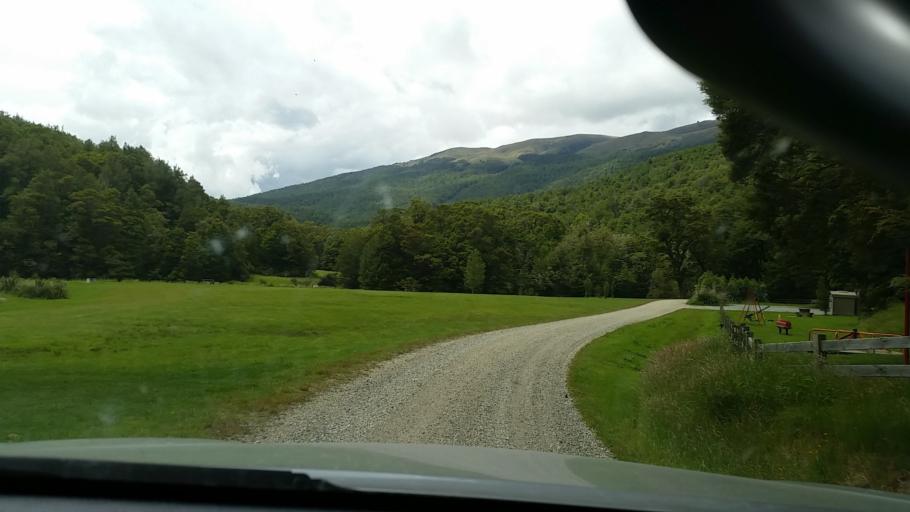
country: NZ
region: Otago
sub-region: Queenstown-Lakes District
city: Kingston
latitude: -45.5545
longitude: 169.0206
